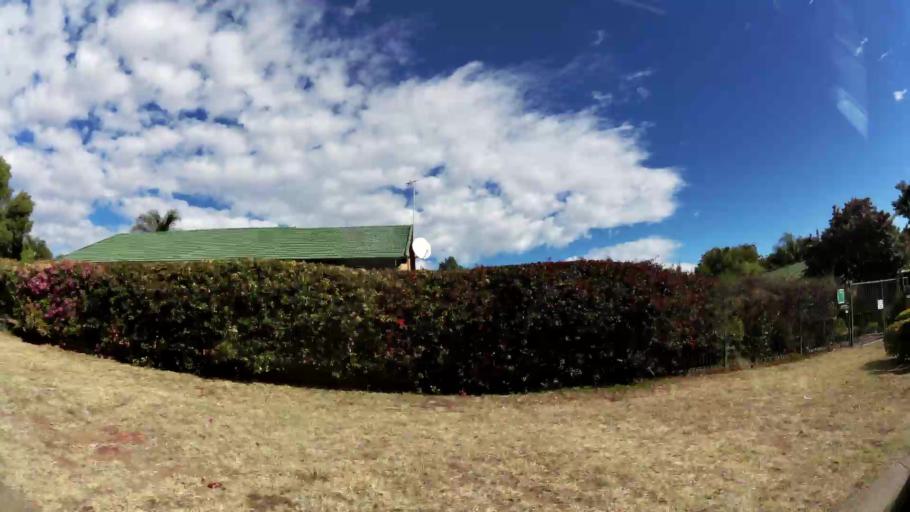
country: ZA
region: Limpopo
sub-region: Waterberg District Municipality
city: Warmbaths
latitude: -24.8709
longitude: 28.2902
